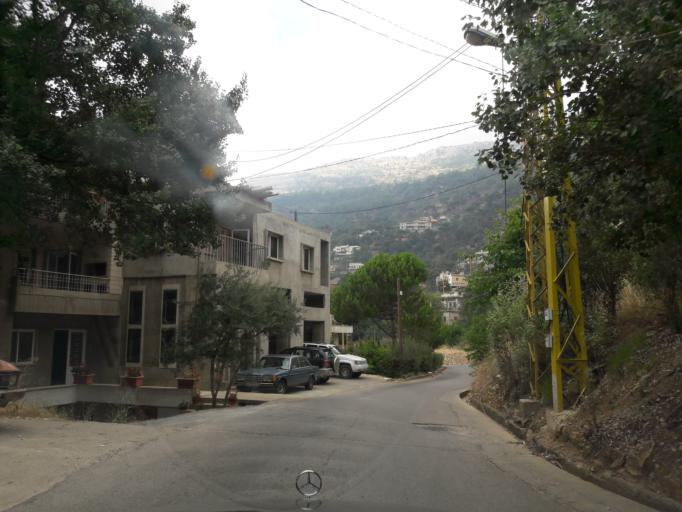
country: LB
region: Beqaa
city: Zahle
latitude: 33.9431
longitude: 35.7998
